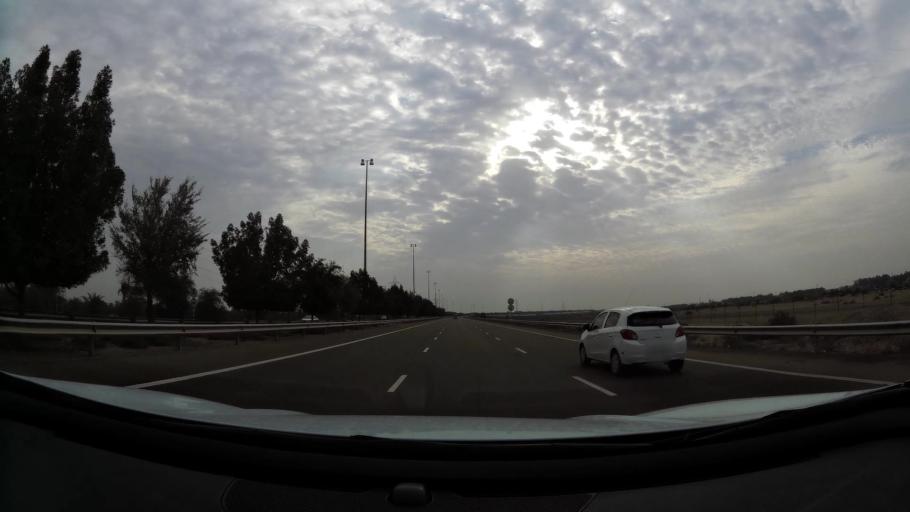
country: AE
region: Abu Dhabi
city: Abu Dhabi
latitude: 24.1884
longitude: 55.0212
